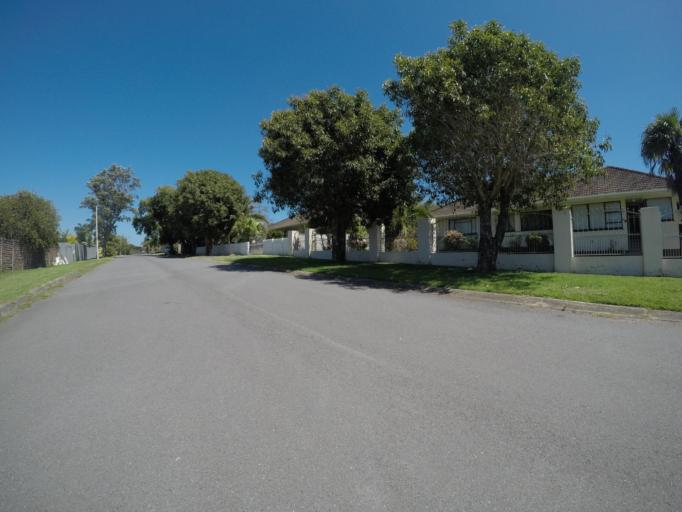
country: ZA
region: Eastern Cape
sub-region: Buffalo City Metropolitan Municipality
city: East London
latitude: -32.9702
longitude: 27.9448
